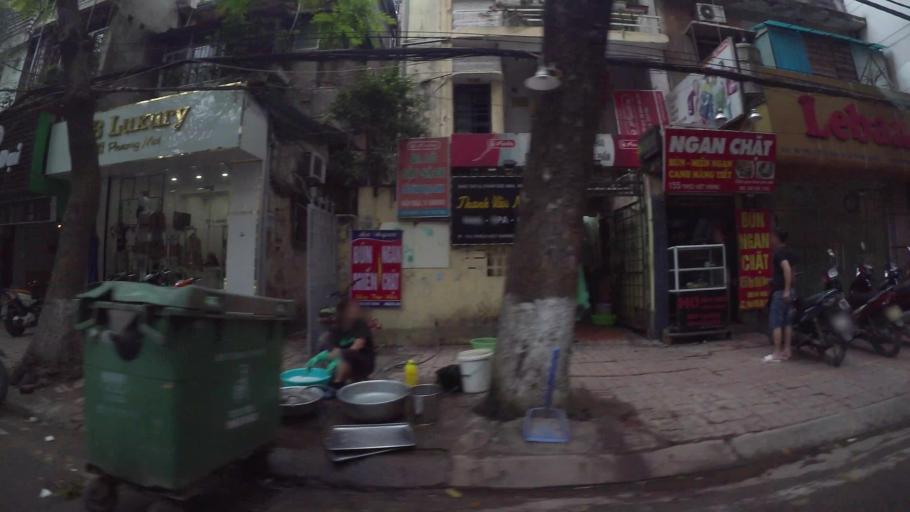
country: VN
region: Ha Noi
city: Hai BaTrung
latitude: 21.0124
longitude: 105.8505
